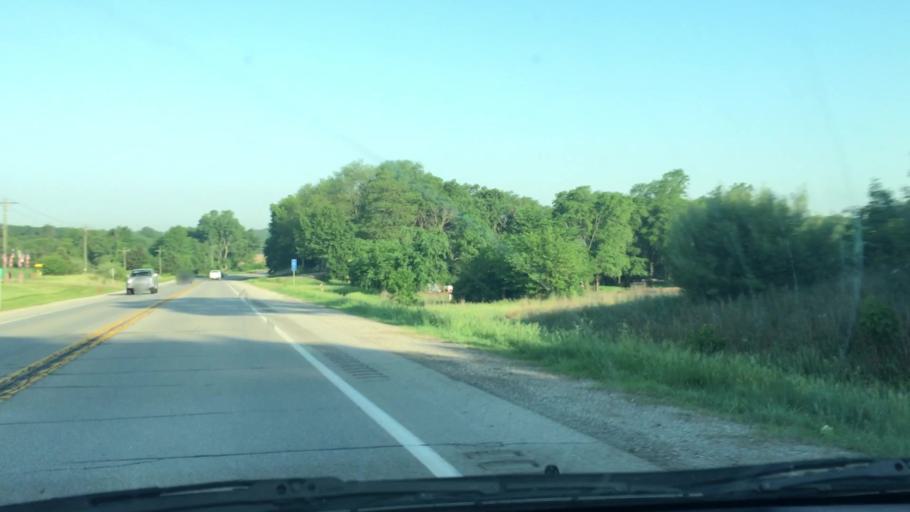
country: US
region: Iowa
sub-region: Johnson County
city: Tiffin
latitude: 41.7114
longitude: -91.6947
